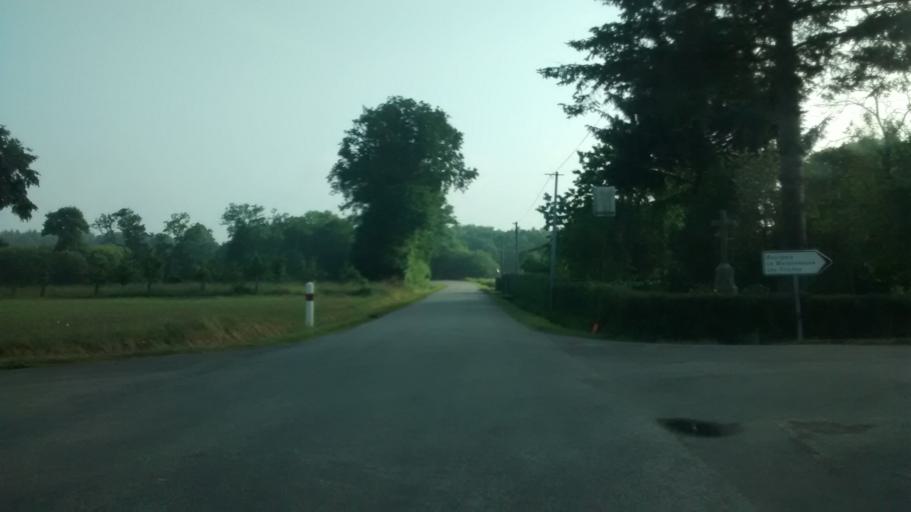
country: FR
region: Brittany
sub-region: Departement du Morbihan
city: Ruffiac
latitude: 47.8368
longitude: -2.2748
